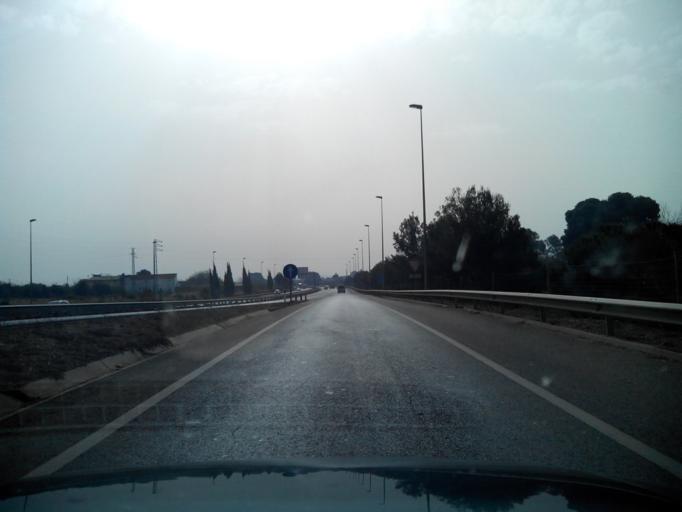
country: ES
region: Catalonia
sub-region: Provincia de Tarragona
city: Reus
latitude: 41.1384
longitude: 1.0993
